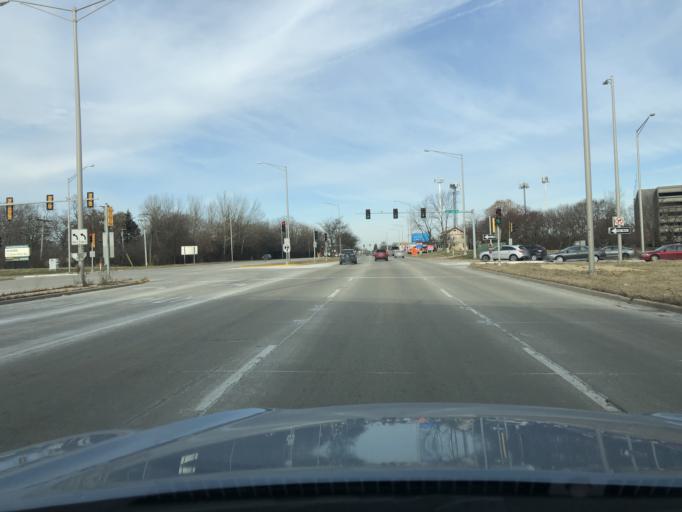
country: US
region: Illinois
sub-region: Cook County
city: Wheeling
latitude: 42.1535
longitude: -87.9146
